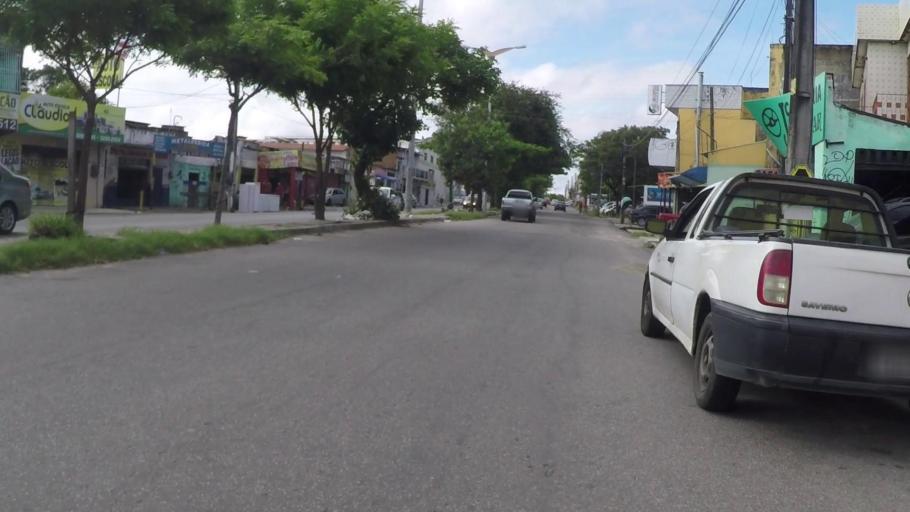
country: BR
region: Ceara
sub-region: Fortaleza
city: Fortaleza
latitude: -3.7257
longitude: -38.5859
